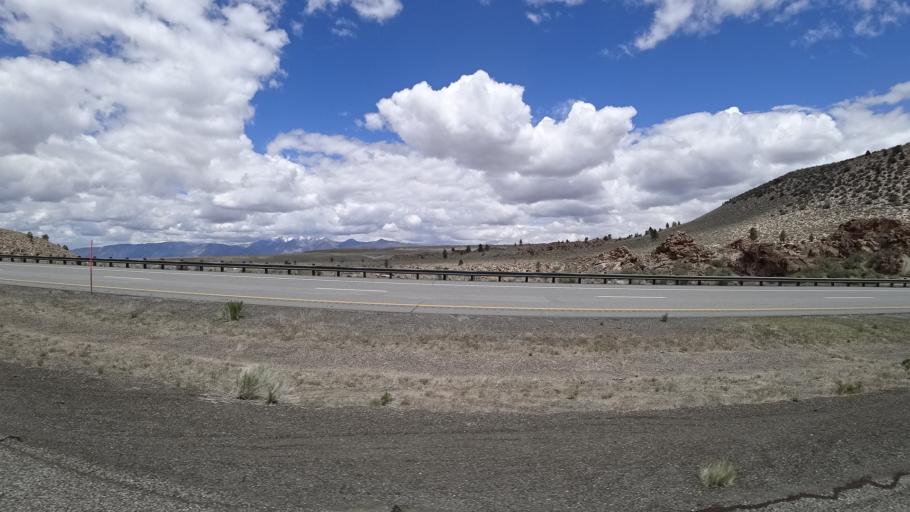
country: US
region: California
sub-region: Mono County
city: Mammoth Lakes
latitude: 37.5741
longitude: -118.7167
